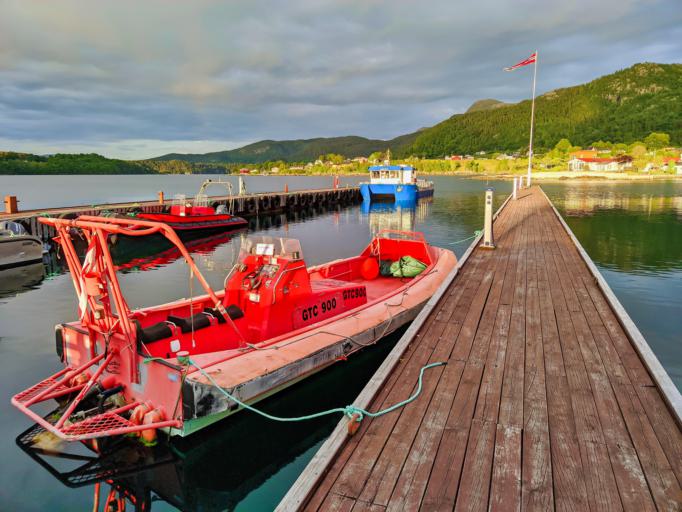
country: NO
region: Hordaland
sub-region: Tysnes
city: Uggdal
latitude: 60.0461
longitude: 5.5249
